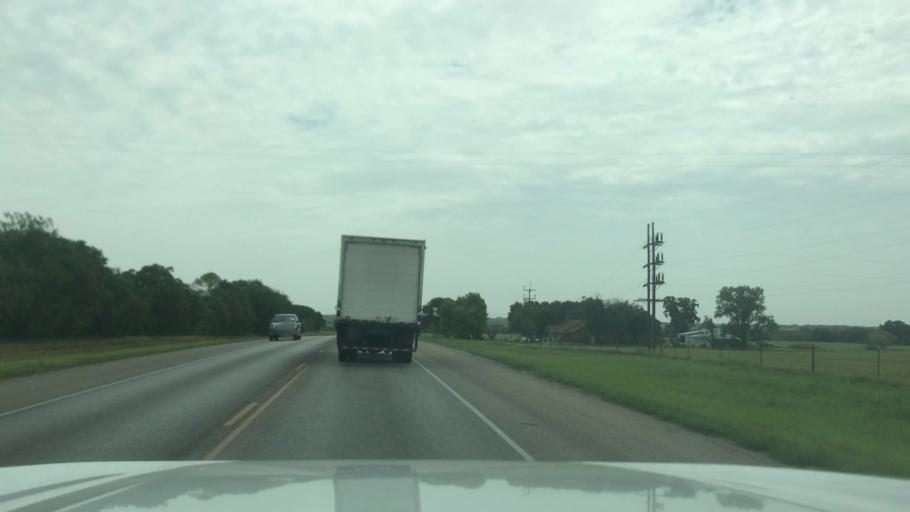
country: US
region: Texas
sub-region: Comanche County
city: De Leon
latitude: 32.0969
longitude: -98.4618
